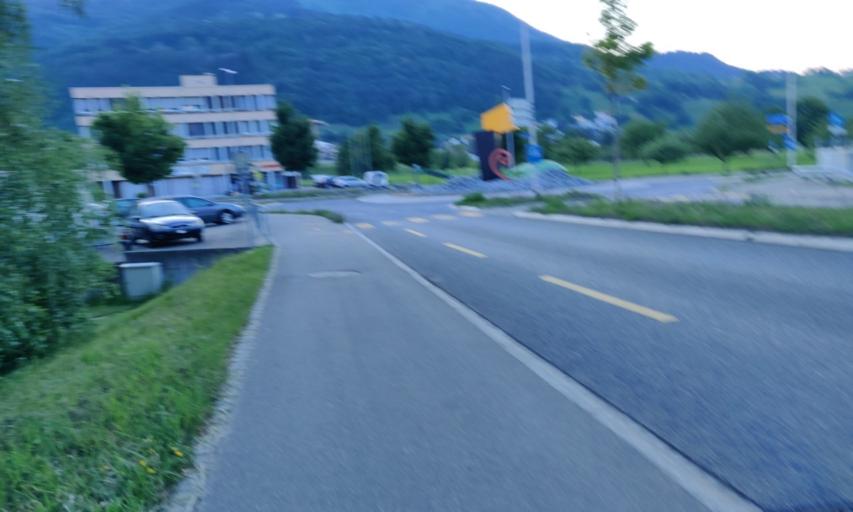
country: LI
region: Balzers
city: Balzers
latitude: 47.0765
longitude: 9.4844
